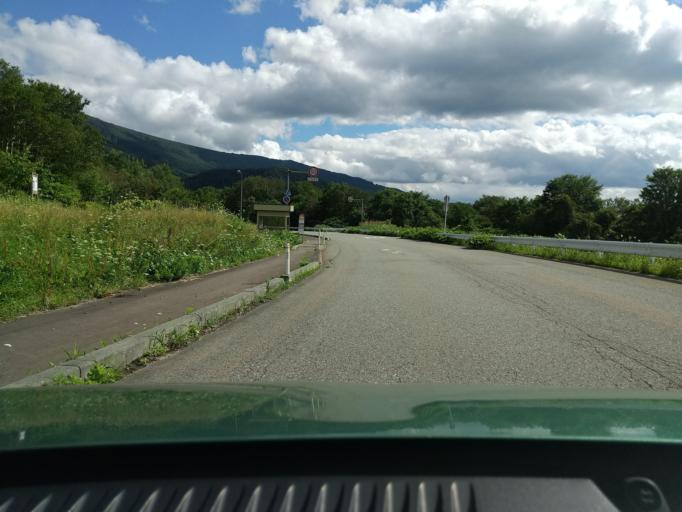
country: JP
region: Iwate
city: Shizukuishi
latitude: 39.7782
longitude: 140.7620
